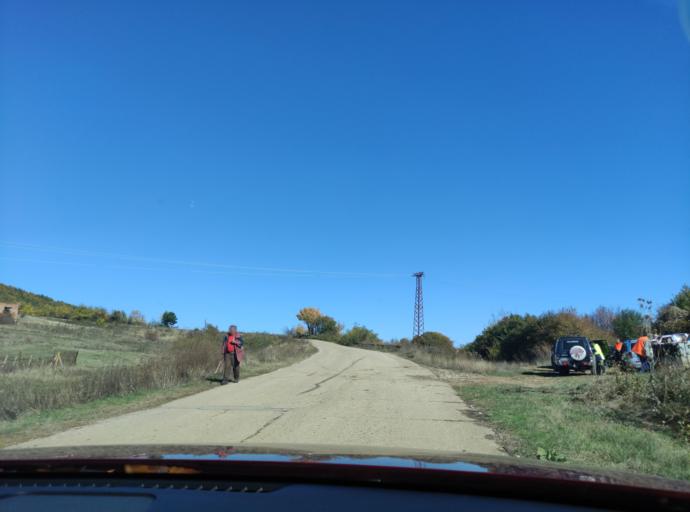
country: BG
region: Montana
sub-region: Obshtina Chiprovtsi
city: Chiprovtsi
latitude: 43.4542
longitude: 23.0478
